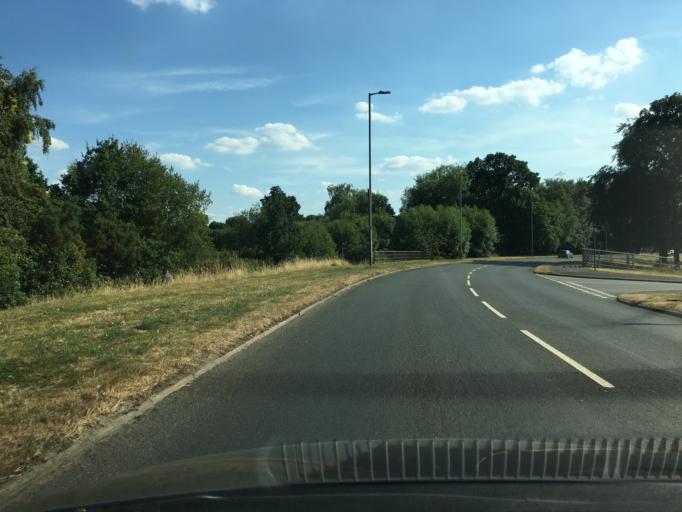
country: GB
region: England
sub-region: Bracknell Forest
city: Bracknell
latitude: 51.3974
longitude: -0.7530
